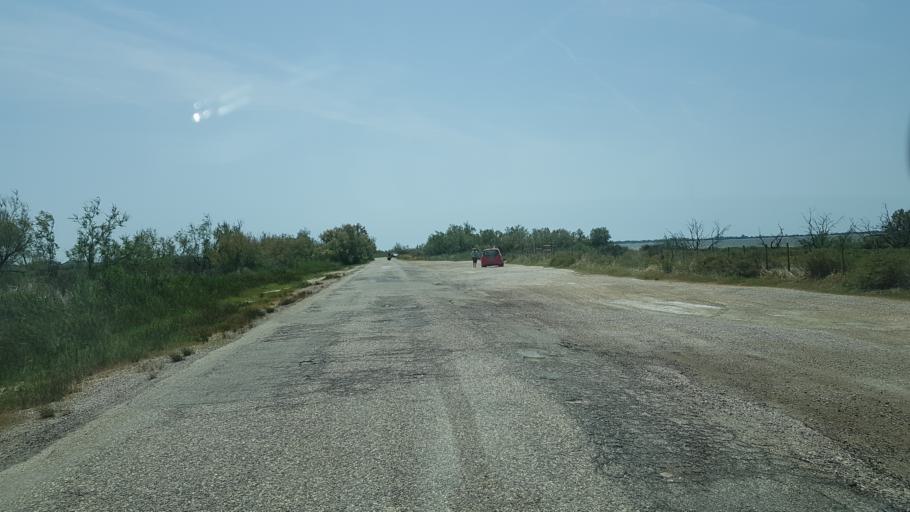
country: FR
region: Provence-Alpes-Cote d'Azur
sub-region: Departement des Bouches-du-Rhone
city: Arles
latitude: 43.5465
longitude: 4.6302
